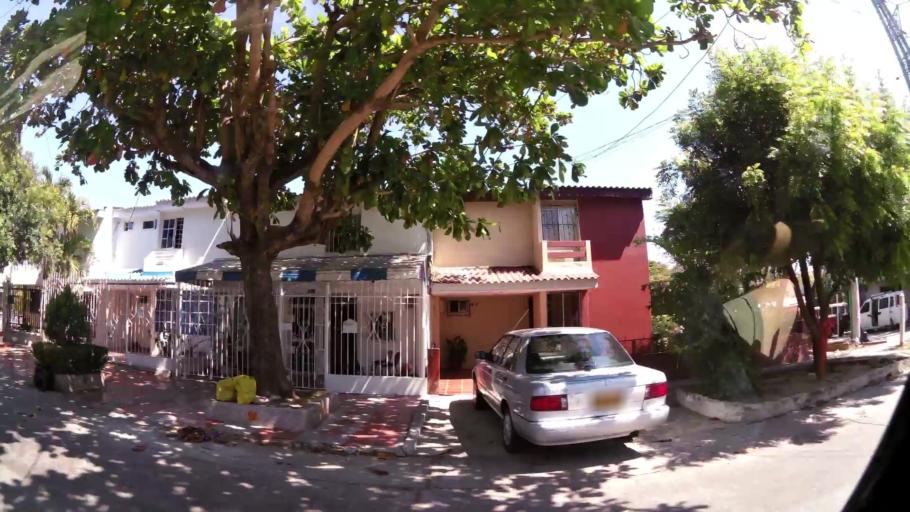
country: CO
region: Atlantico
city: Barranquilla
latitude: 11.0104
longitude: -74.7950
